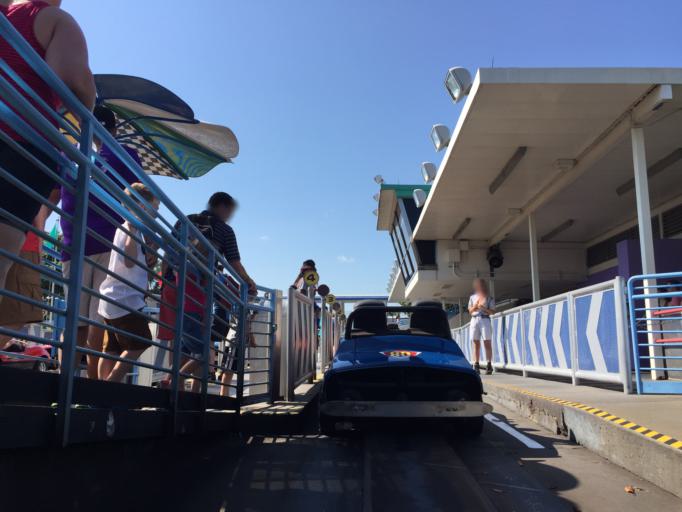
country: US
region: Florida
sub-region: Orange County
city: Bay Hill
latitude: 28.4196
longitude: -81.5793
